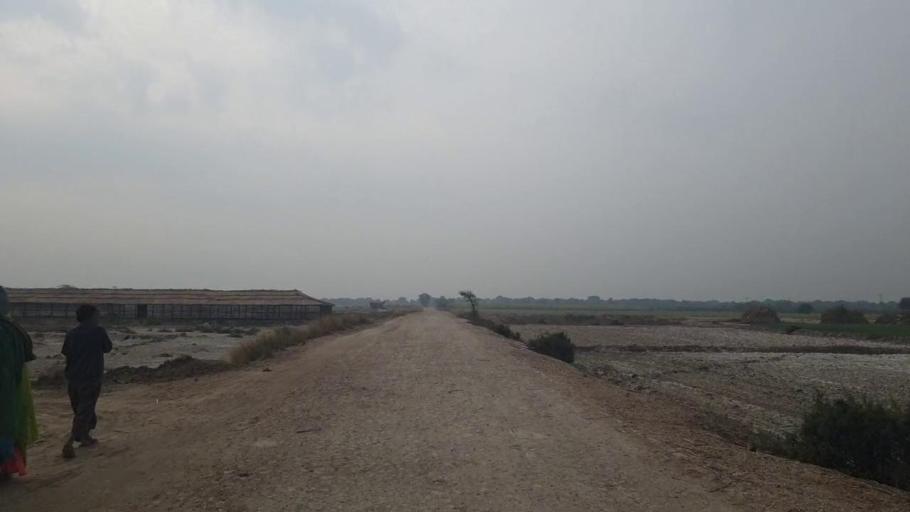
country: PK
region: Sindh
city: Tando Adam
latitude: 25.7345
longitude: 68.6824
